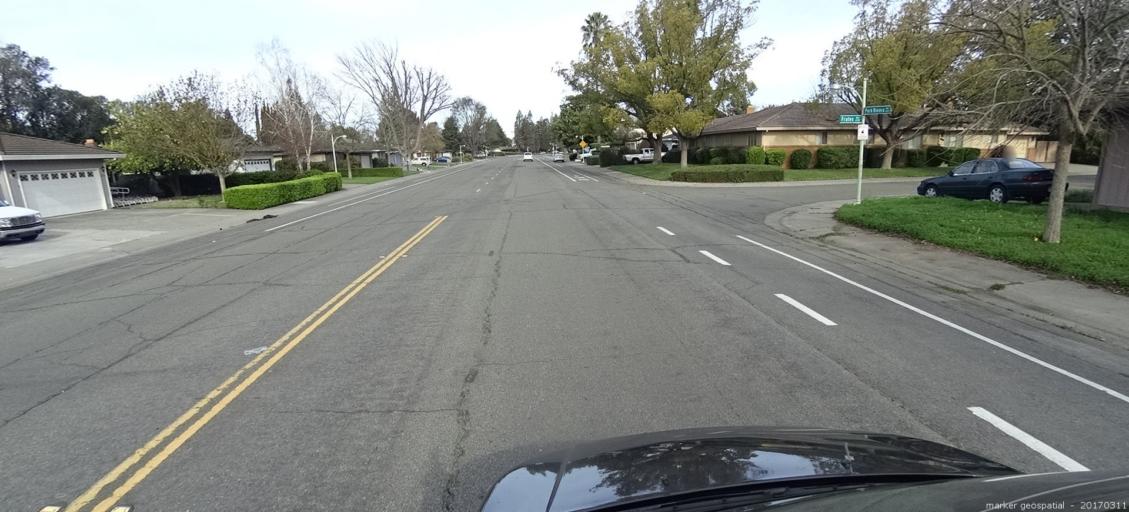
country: US
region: California
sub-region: Yolo County
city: West Sacramento
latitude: 38.5033
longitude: -121.5480
